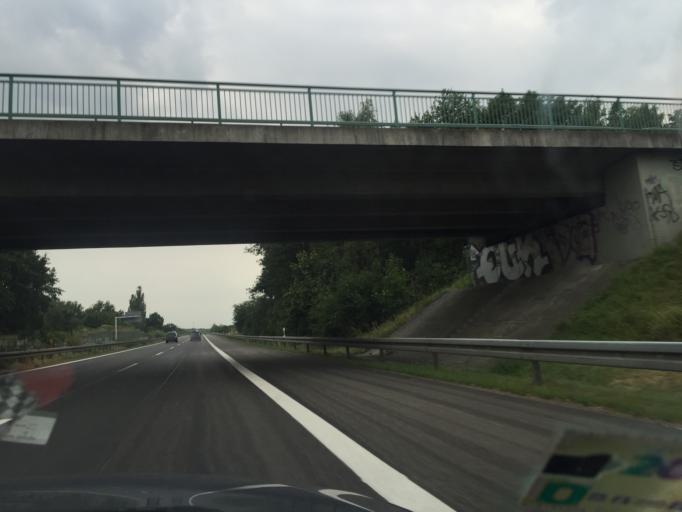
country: DE
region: Brandenburg
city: Bernau bei Berlin
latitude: 52.6822
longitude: 13.5624
